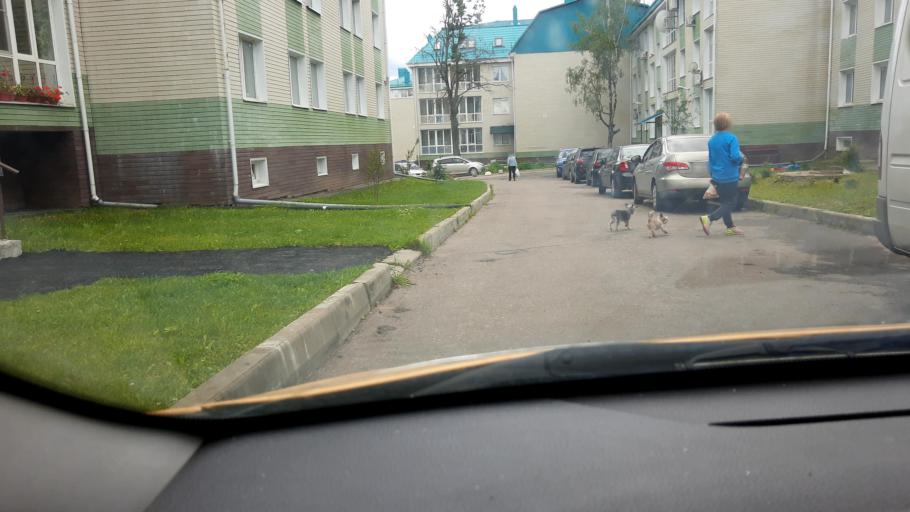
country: RU
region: Moskovskaya
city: Kokoshkino
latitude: 55.5365
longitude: 37.1599
